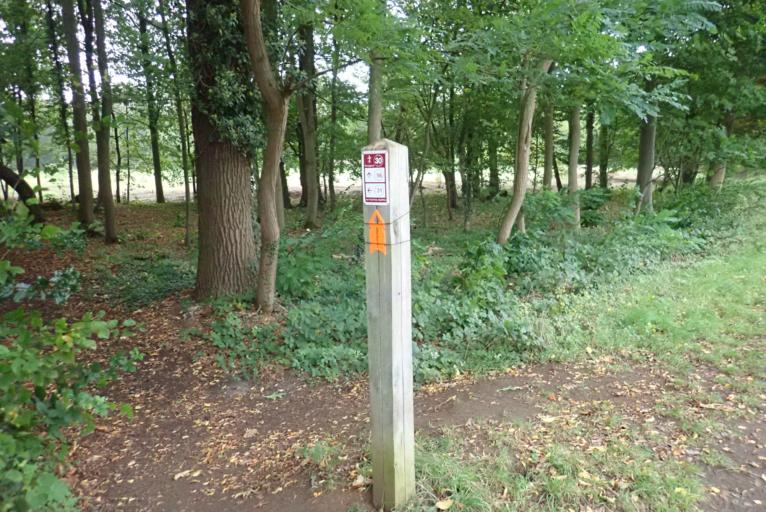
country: BE
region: Flanders
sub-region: Provincie Antwerpen
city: Hulshout
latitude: 51.0616
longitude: 4.7844
